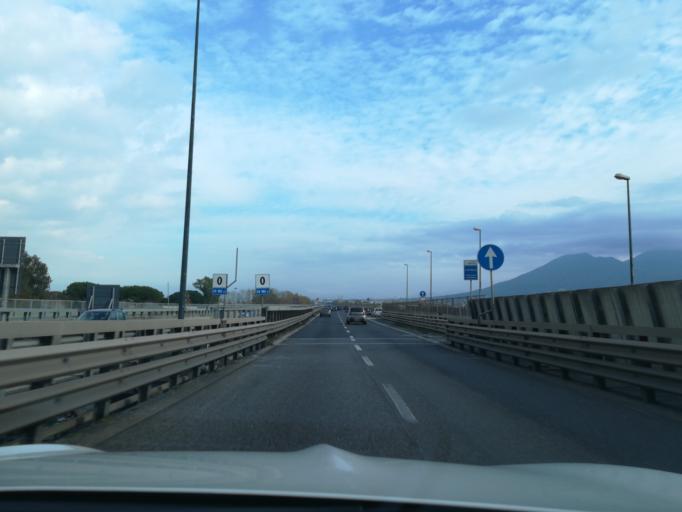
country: IT
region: Campania
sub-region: Provincia di Napoli
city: Arpino
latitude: 40.8644
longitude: 14.2990
